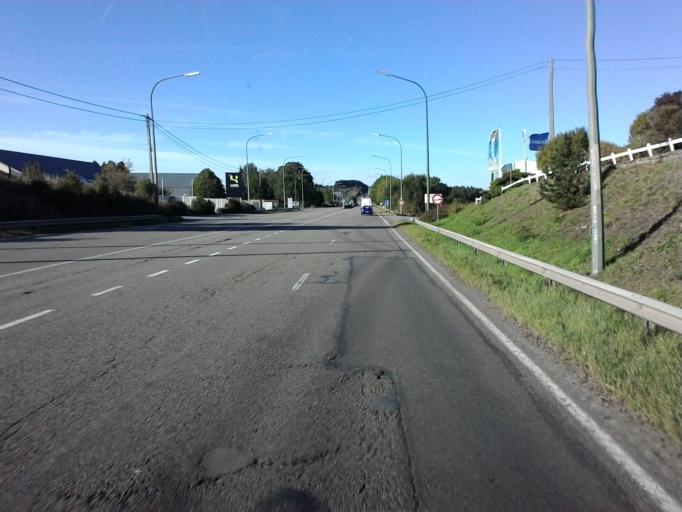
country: BE
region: Wallonia
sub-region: Province du Luxembourg
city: Fauvillers
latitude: 49.8991
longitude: 5.7001
